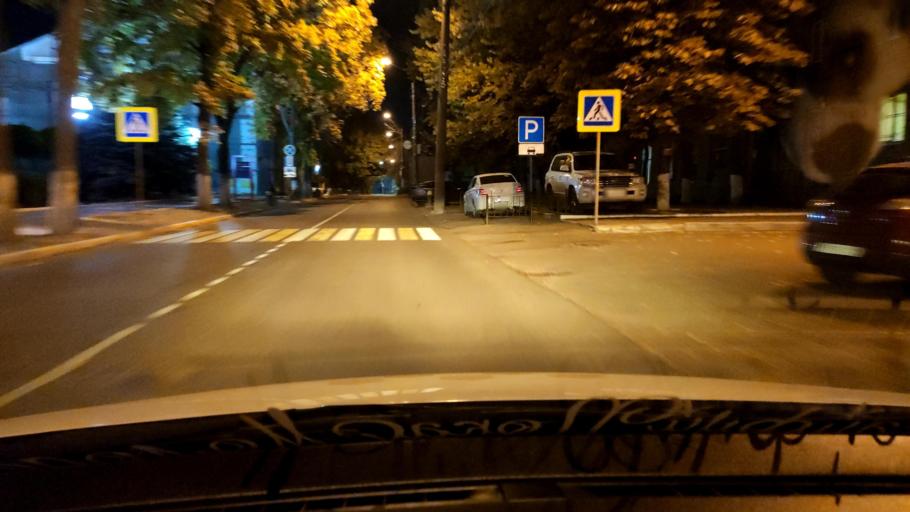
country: RU
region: Voronezj
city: Voronezh
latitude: 51.6853
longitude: 39.1700
